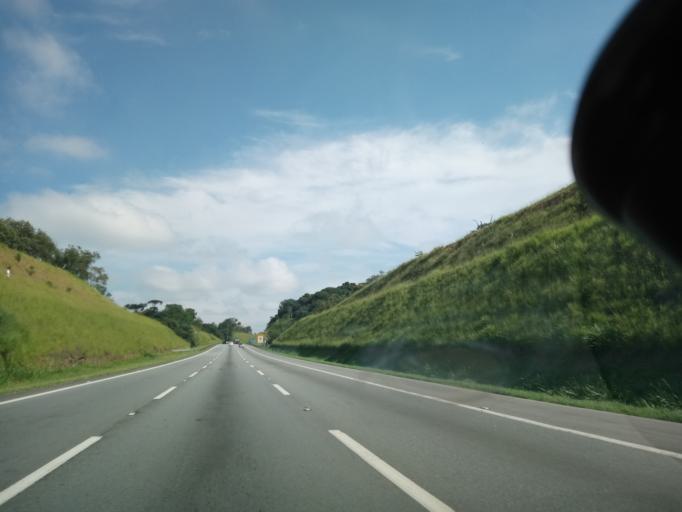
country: BR
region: Sao Paulo
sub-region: Embu
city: Embu
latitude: -23.6773
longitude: -46.8223
